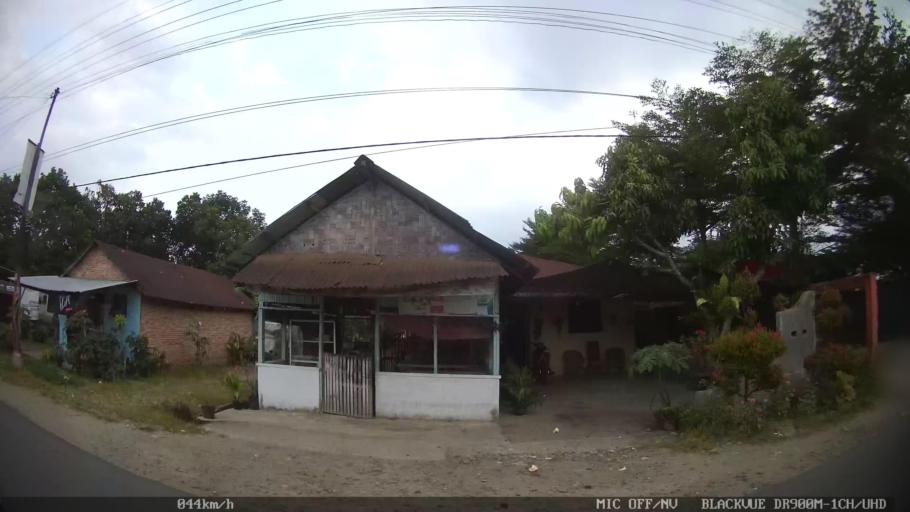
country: ID
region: North Sumatra
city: Sunggal
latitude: 3.5610
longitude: 98.5696
